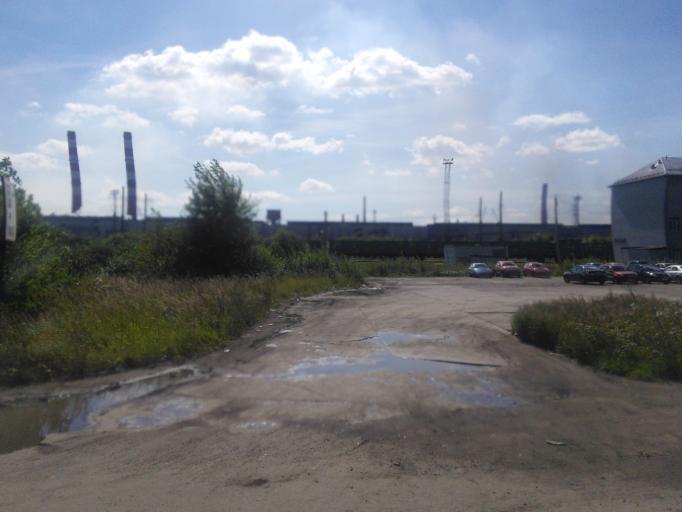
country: RU
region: Vologda
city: Cherepovets
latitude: 59.1535
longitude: 37.8832
